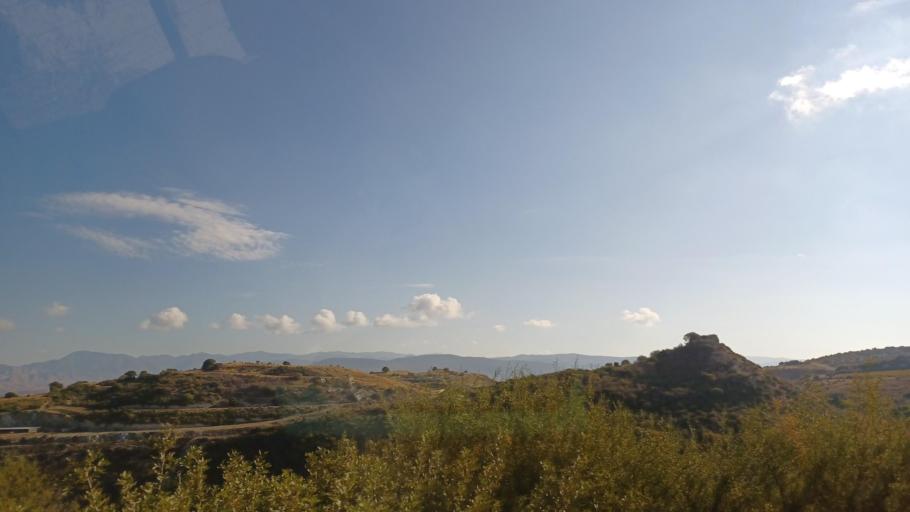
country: CY
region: Pafos
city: Polis
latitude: 35.0164
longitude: 32.3966
